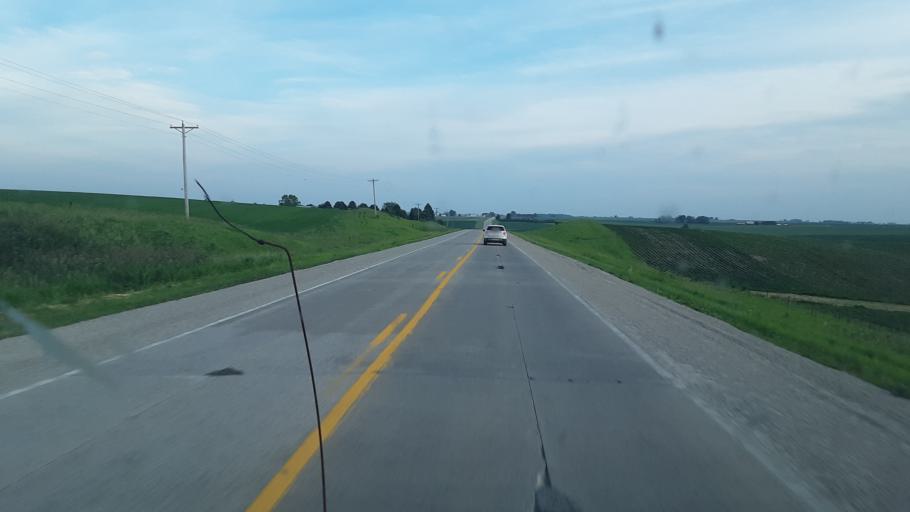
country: US
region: Iowa
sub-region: Benton County
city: Belle Plaine
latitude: 41.8148
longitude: -92.2789
